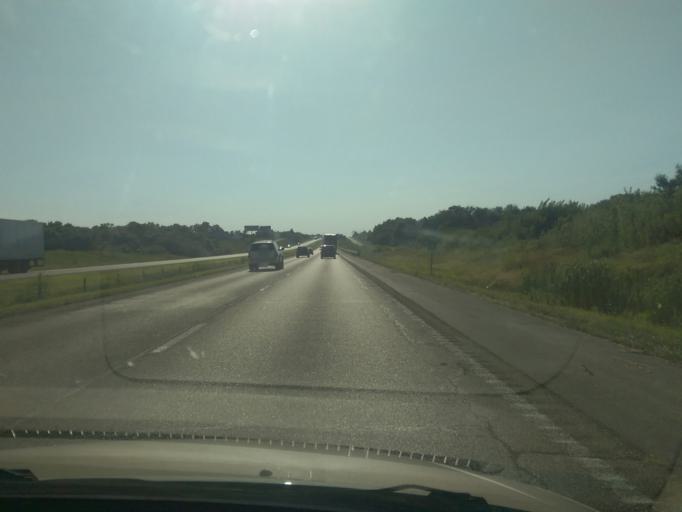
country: US
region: Missouri
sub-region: Lafayette County
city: Higginsville
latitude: 39.0021
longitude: -93.7830
